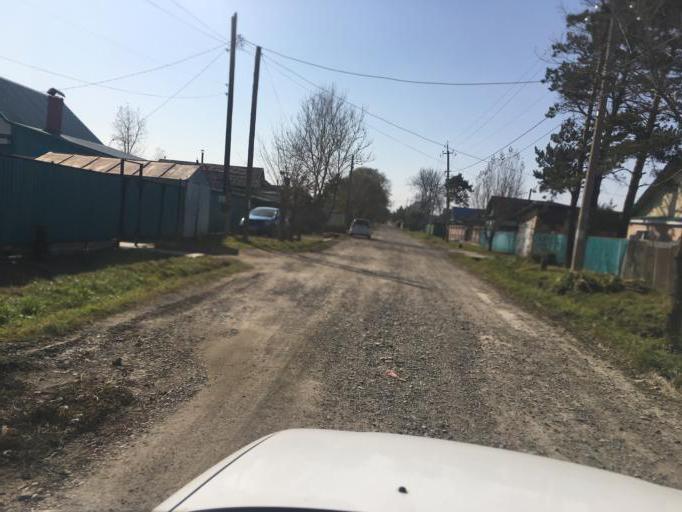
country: RU
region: Primorskiy
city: Dal'nerechensk
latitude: 45.9291
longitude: 133.7462
